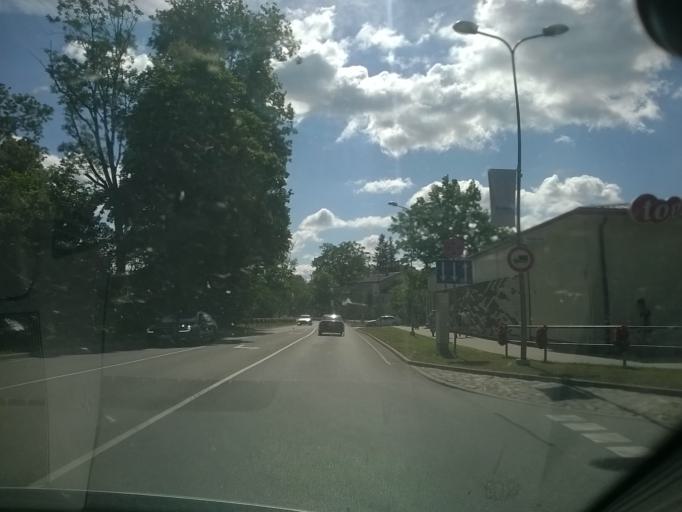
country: LV
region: Aluksnes Rajons
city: Aluksne
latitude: 57.4265
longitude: 27.0411
